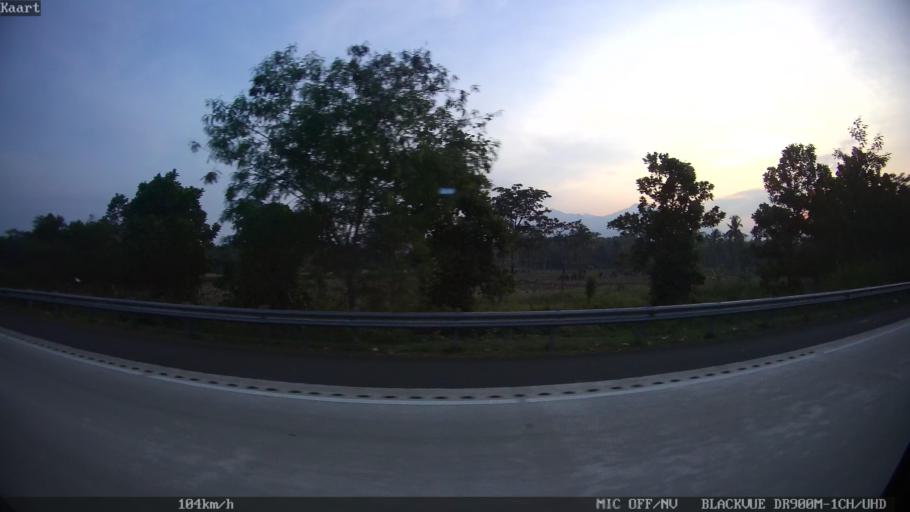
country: ID
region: Lampung
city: Penengahan
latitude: -5.7491
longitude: 105.7050
